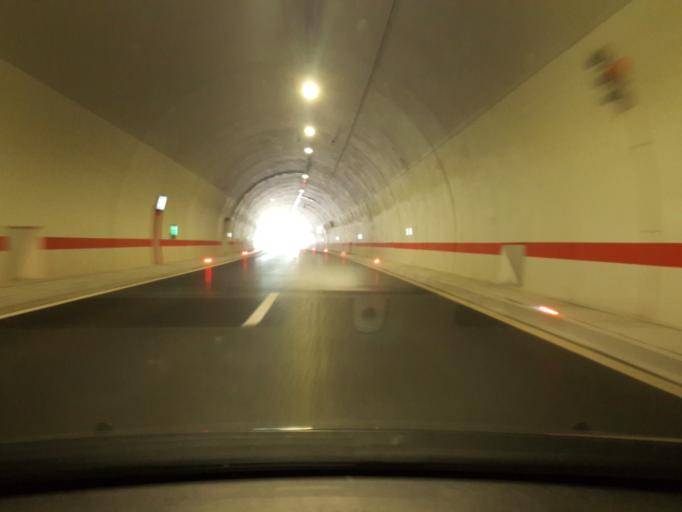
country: RS
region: Central Serbia
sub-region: Pirotski Okrug
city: Pirot
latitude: 43.1625
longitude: 22.5751
